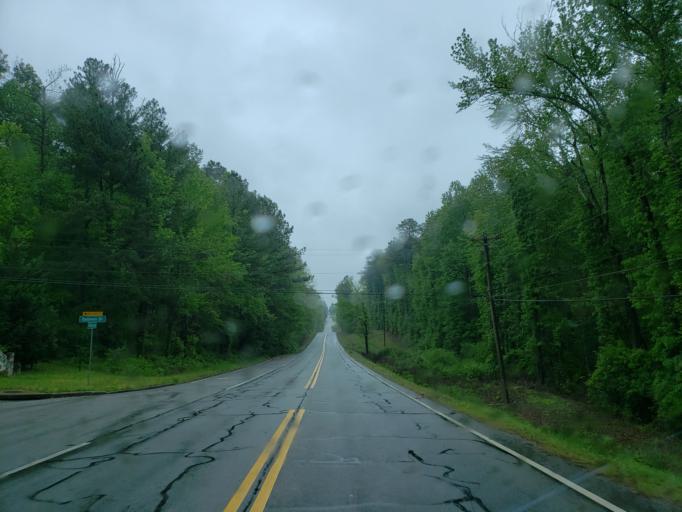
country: US
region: Georgia
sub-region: Paulding County
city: Dallas
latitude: 33.8290
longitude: -84.8735
